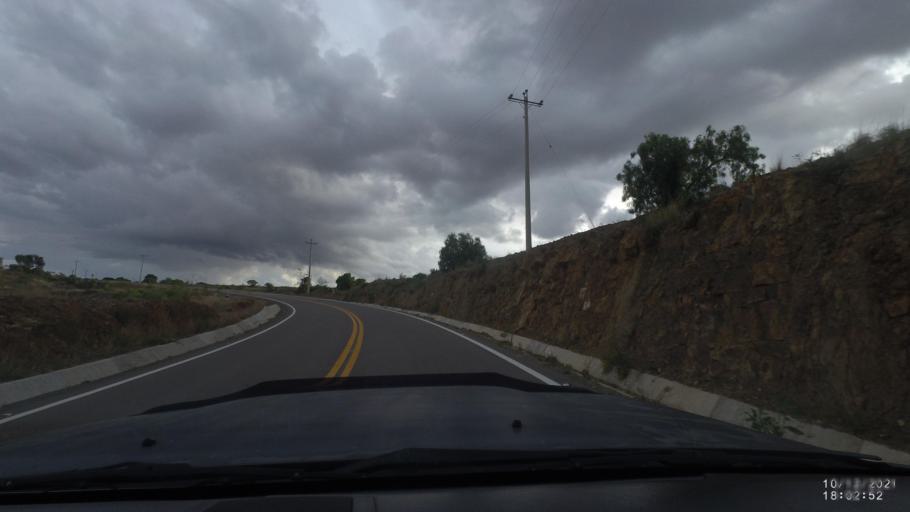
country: BO
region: Cochabamba
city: Cliza
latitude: -17.7545
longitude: -65.9200
